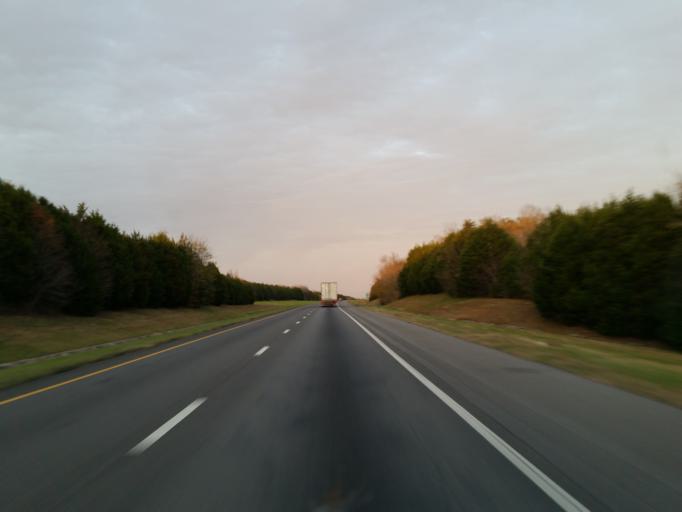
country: US
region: Alabama
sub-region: Sumter County
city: Livingston
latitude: 32.6492
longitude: -88.1923
